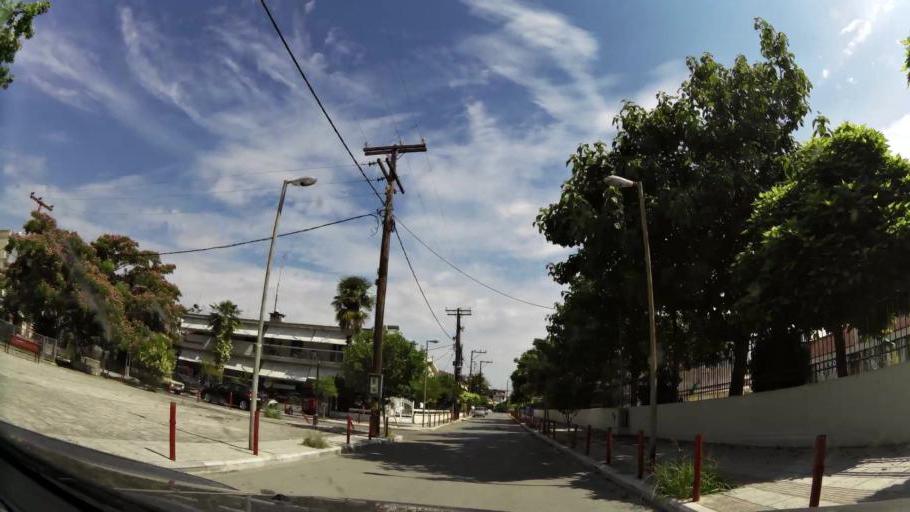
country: GR
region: Central Macedonia
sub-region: Nomos Pierias
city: Katerini
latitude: 40.2649
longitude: 22.4946
